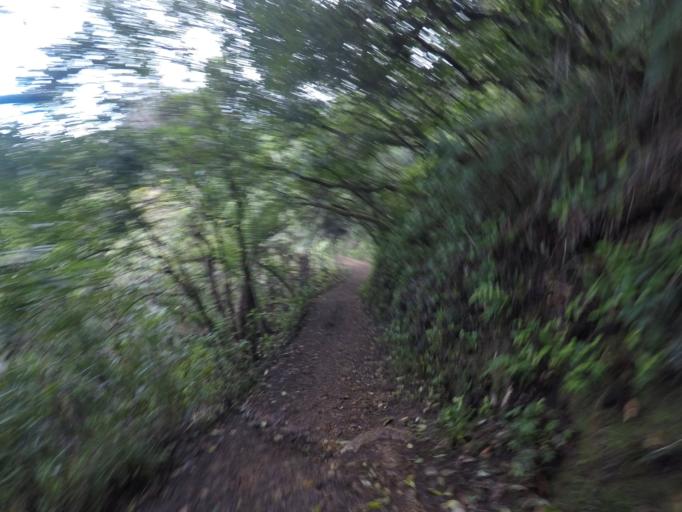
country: NZ
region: Bay of Plenty
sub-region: Western Bay of Plenty District
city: Waihi Beach
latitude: -37.3909
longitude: 175.9400
